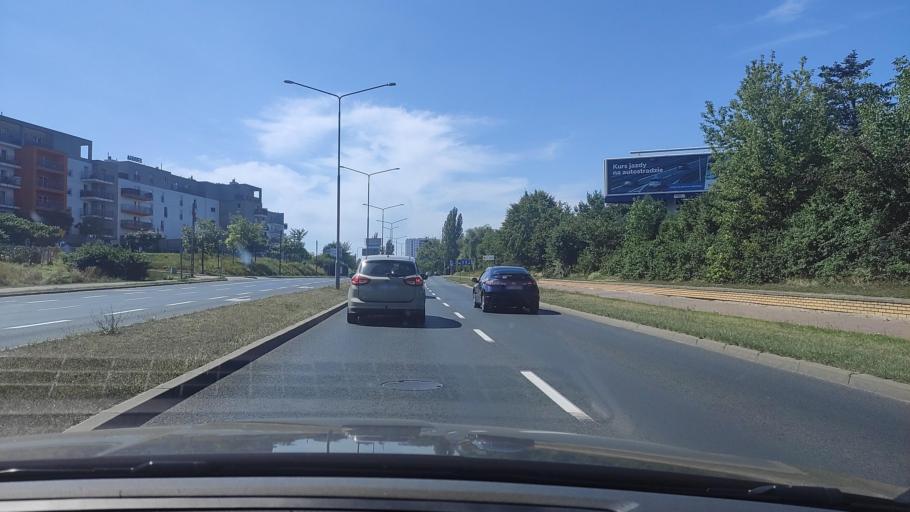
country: PL
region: Greater Poland Voivodeship
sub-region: Poznan
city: Poznan
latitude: 52.4306
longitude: 16.9566
